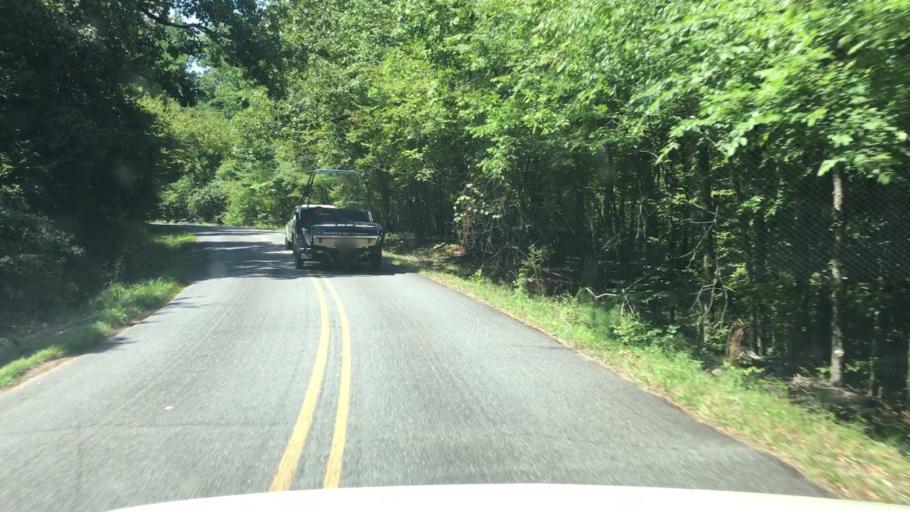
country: US
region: Arkansas
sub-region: Garland County
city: Piney
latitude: 34.5347
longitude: -93.3392
